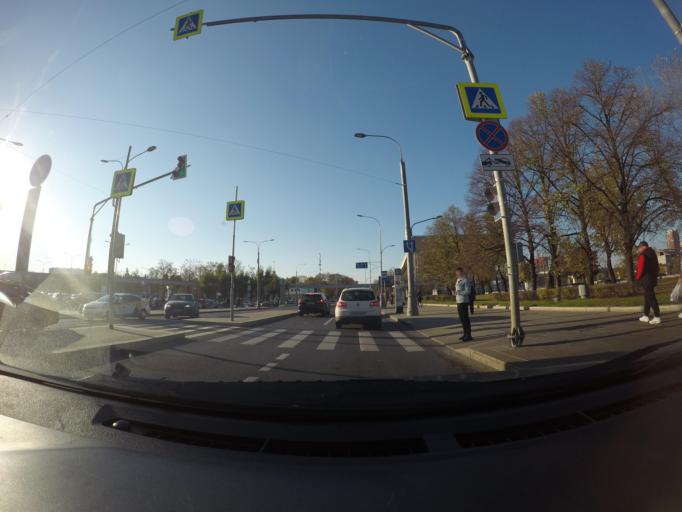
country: RU
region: Moscow
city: Rostokino
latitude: 55.8273
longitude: 37.6451
